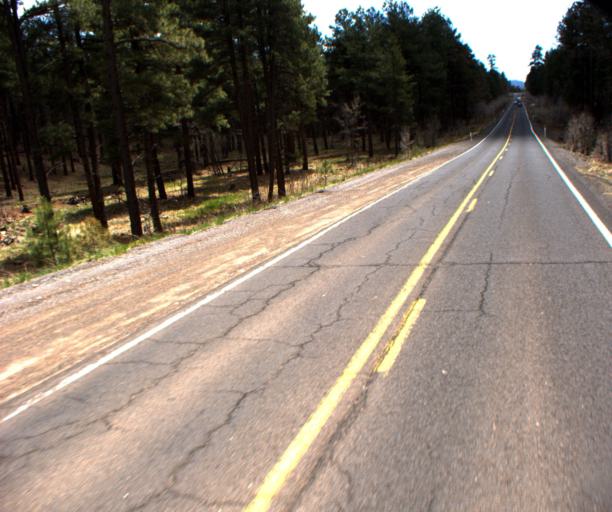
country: US
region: Arizona
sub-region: Coconino County
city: Kachina Village
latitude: 35.0949
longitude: -111.7327
